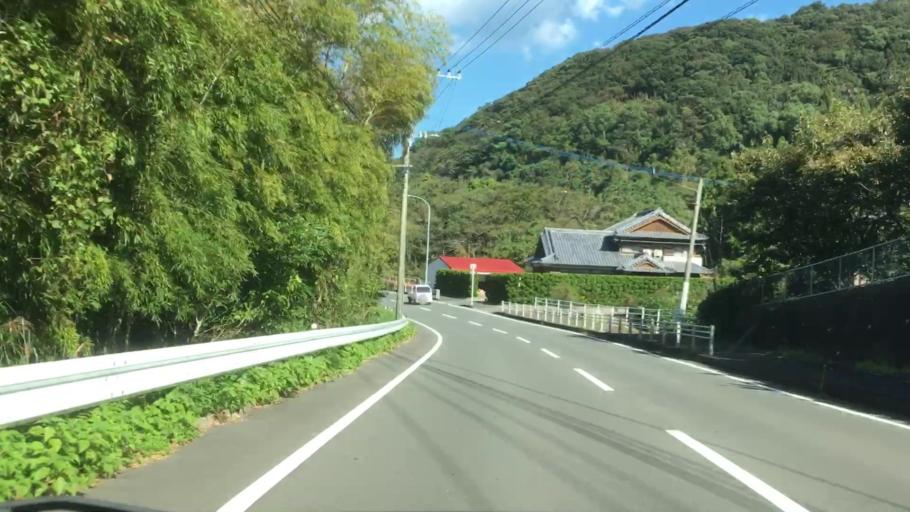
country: JP
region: Nagasaki
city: Sasebo
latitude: 33.0075
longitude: 129.6570
